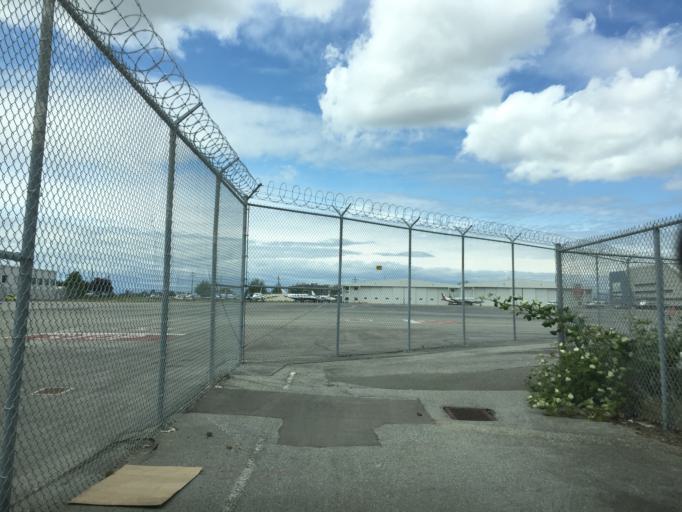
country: CA
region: British Columbia
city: Richmond
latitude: 49.1796
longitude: -123.1702
